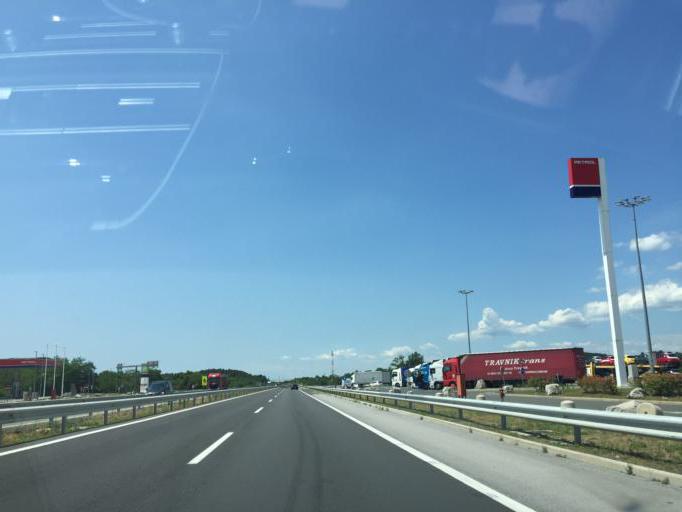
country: SI
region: Divaca
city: Divaca
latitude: 45.7036
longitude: 13.9419
